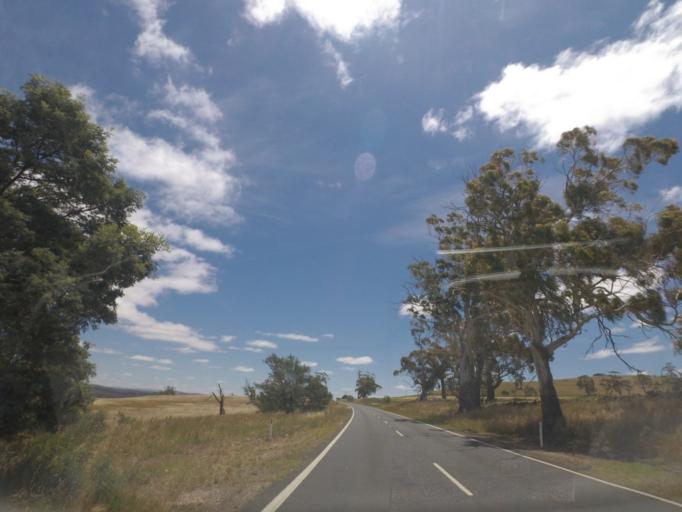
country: AU
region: Victoria
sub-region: Mount Alexander
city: Castlemaine
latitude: -37.2715
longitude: 144.1446
